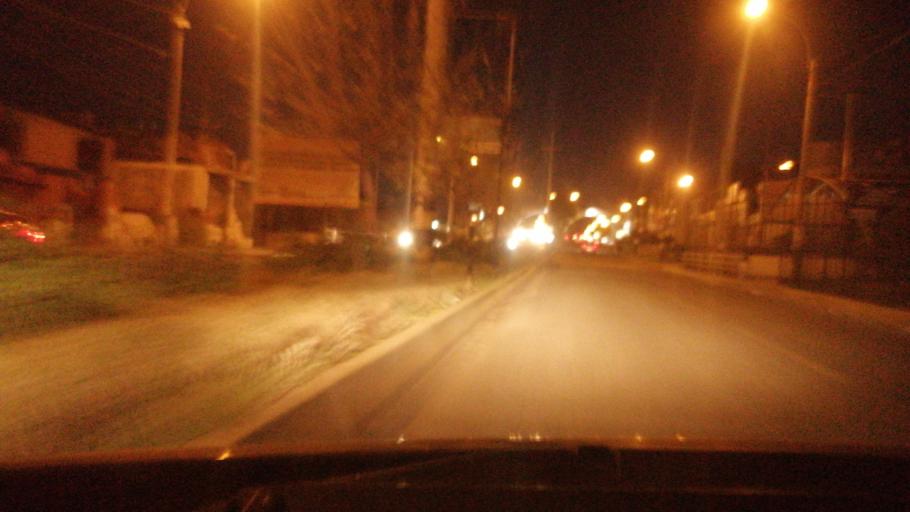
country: PE
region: Arequipa
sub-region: Provincia de Arequipa
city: Socabaya
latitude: -16.4349
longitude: -71.5313
